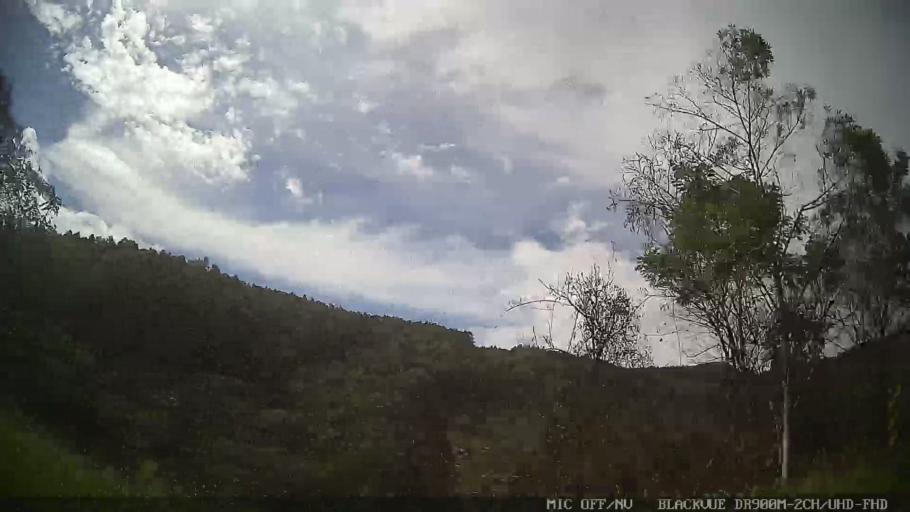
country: BR
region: Sao Paulo
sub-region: Santa Branca
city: Santa Branca
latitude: -23.5249
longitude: -45.8040
